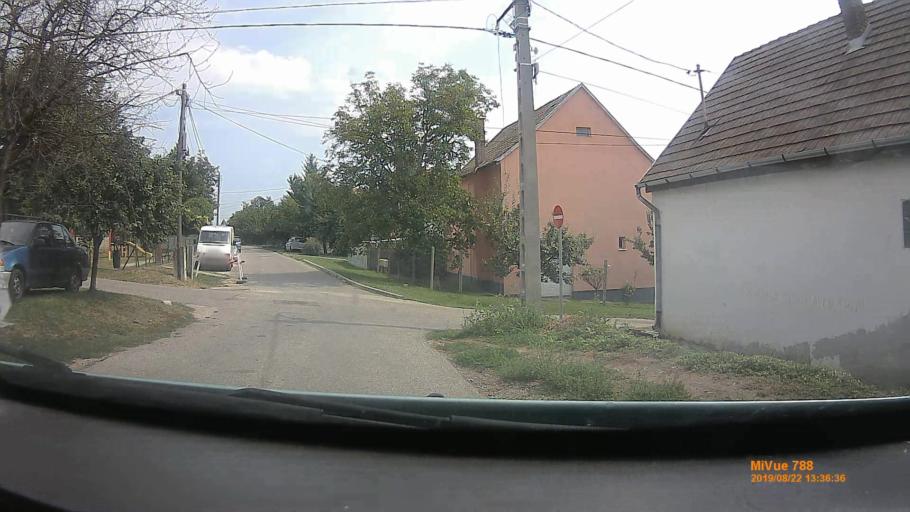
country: HU
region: Komarom-Esztergom
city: Piliscsev
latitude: 47.6638
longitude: 18.8067
